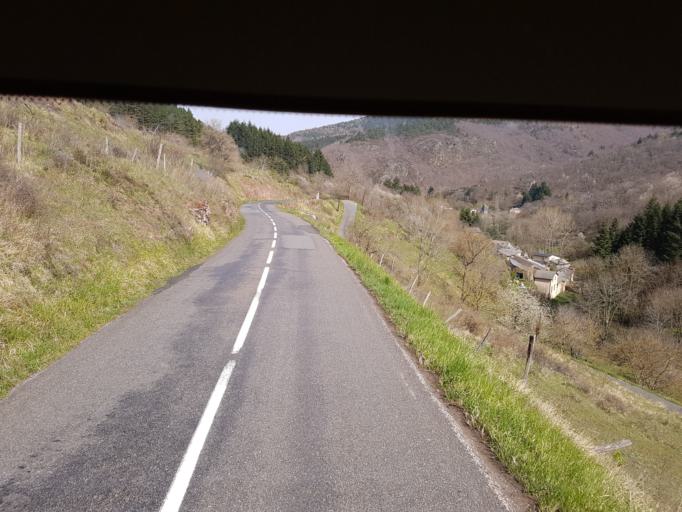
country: FR
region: Languedoc-Roussillon
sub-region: Departement de la Lozere
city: Meyrueis
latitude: 44.2157
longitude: 3.5310
